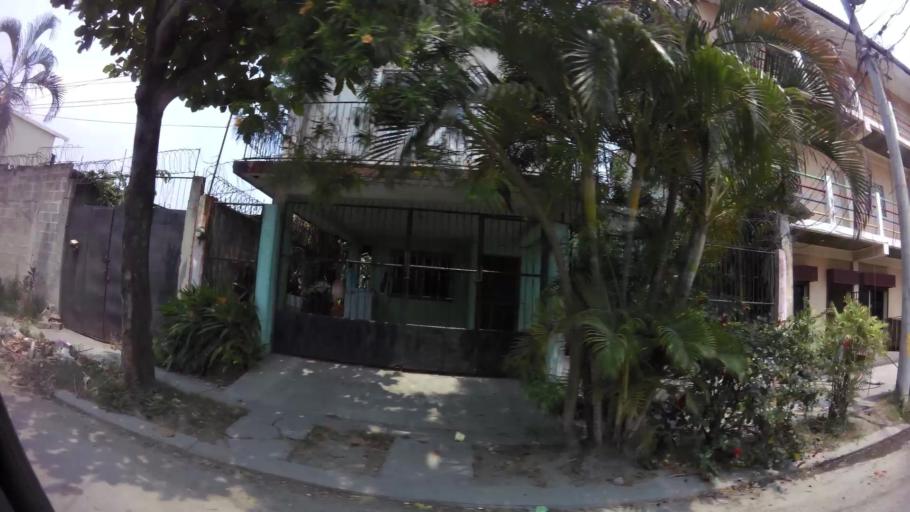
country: HN
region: Cortes
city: San Pedro Sula
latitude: 15.4914
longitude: -88.0016
